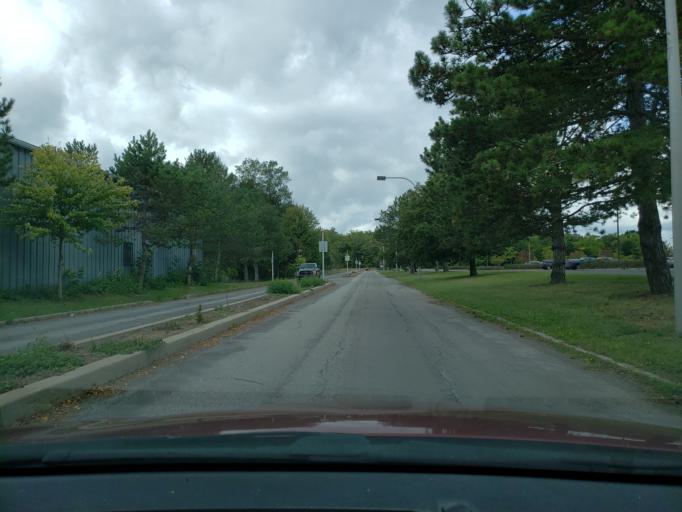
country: US
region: New York
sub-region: Monroe County
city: North Gates
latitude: 43.1481
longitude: -77.7374
